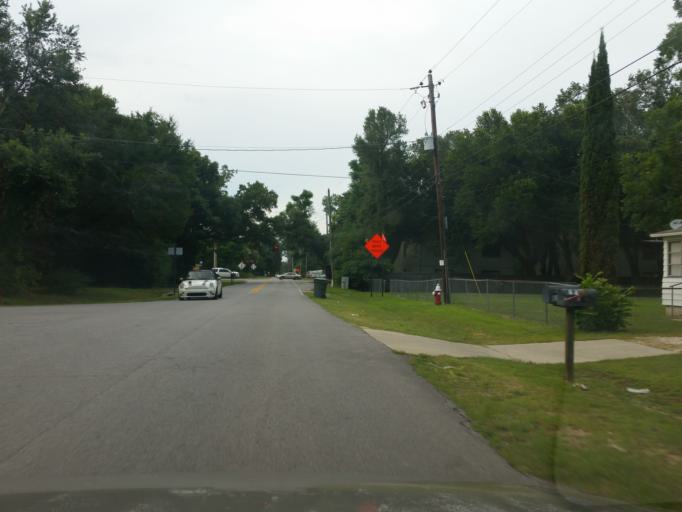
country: US
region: Florida
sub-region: Escambia County
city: Ferry Pass
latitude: 30.5094
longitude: -87.2271
